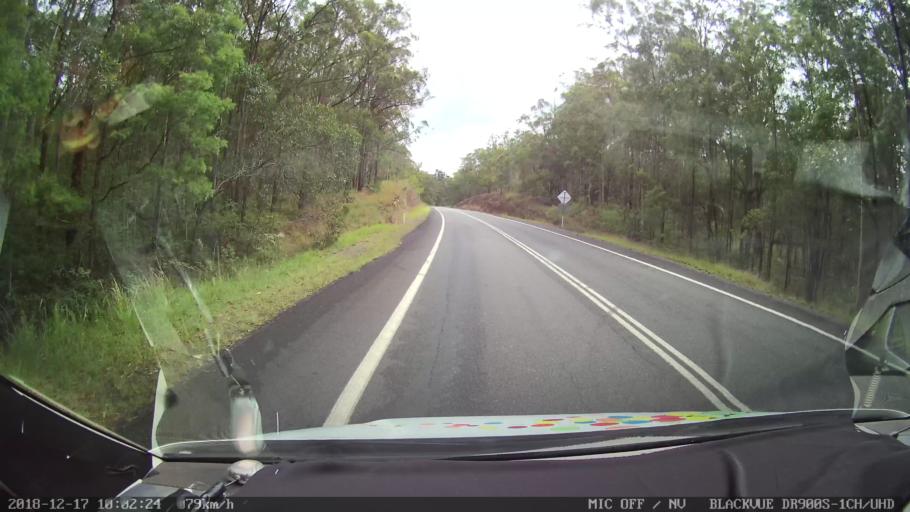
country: AU
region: New South Wales
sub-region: Tenterfield Municipality
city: Carrolls Creek
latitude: -28.9028
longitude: 152.4512
